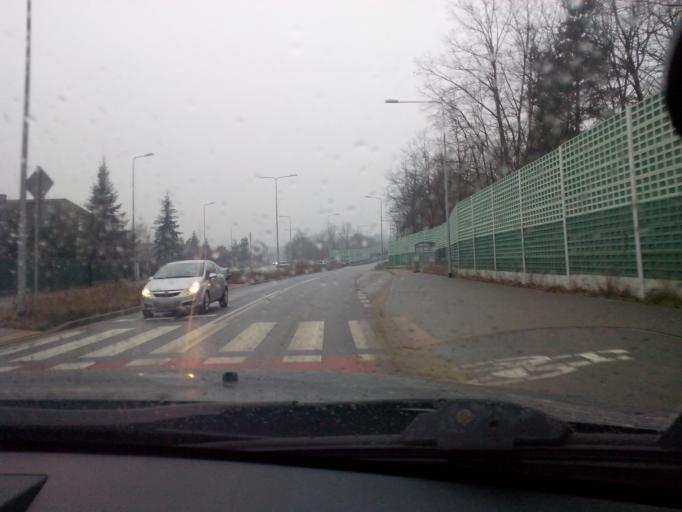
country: PL
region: Masovian Voivodeship
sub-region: Warszawa
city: Bialoleka
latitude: 52.3518
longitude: 20.9820
